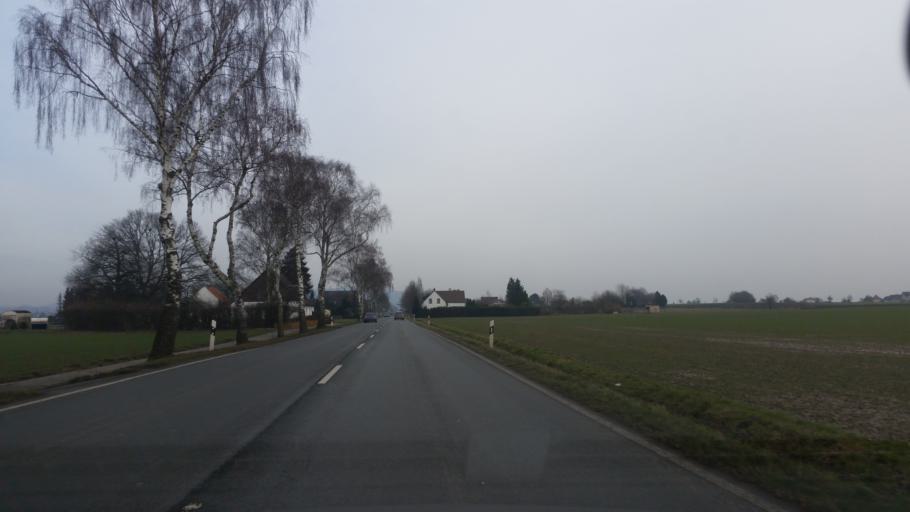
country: DE
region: North Rhine-Westphalia
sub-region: Regierungsbezirk Detmold
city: Lemgo
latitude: 52.0180
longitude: 8.8642
